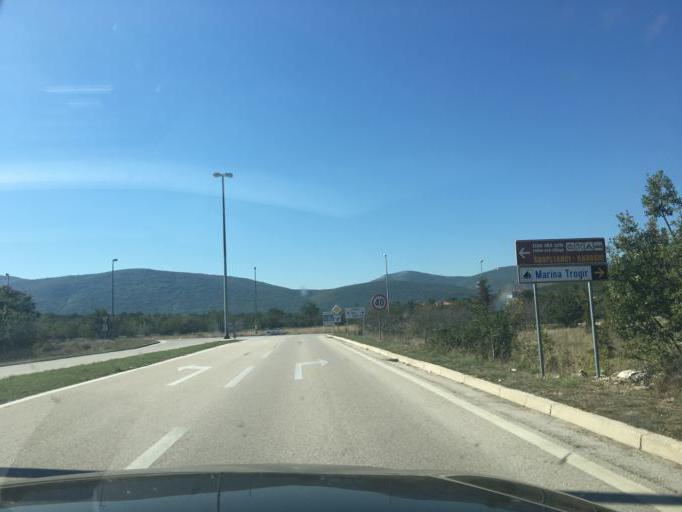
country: HR
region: Splitsko-Dalmatinska
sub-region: Grad Trogir
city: Trogir
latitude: 43.6126
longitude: 16.2304
